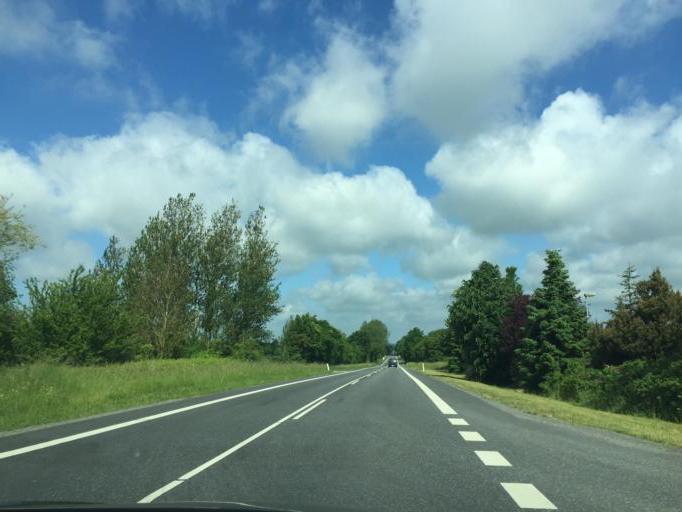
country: DK
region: South Denmark
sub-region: Assens Kommune
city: Arup
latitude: 55.4301
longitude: 10.0142
